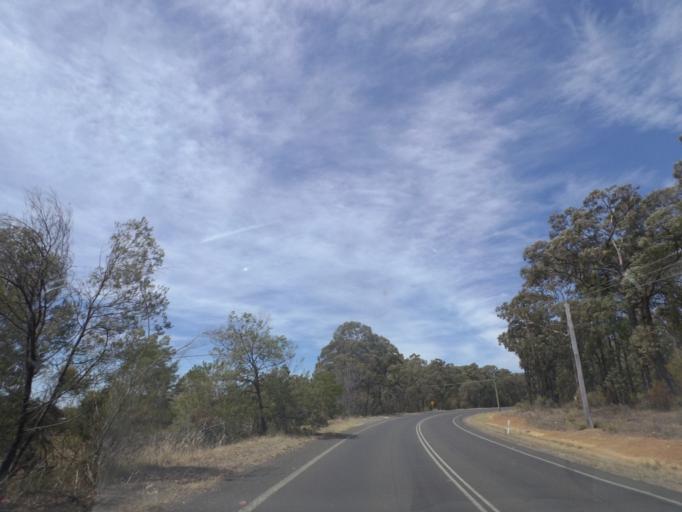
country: AU
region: New South Wales
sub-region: Wollondilly
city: Buxton
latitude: -34.3137
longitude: 150.5791
